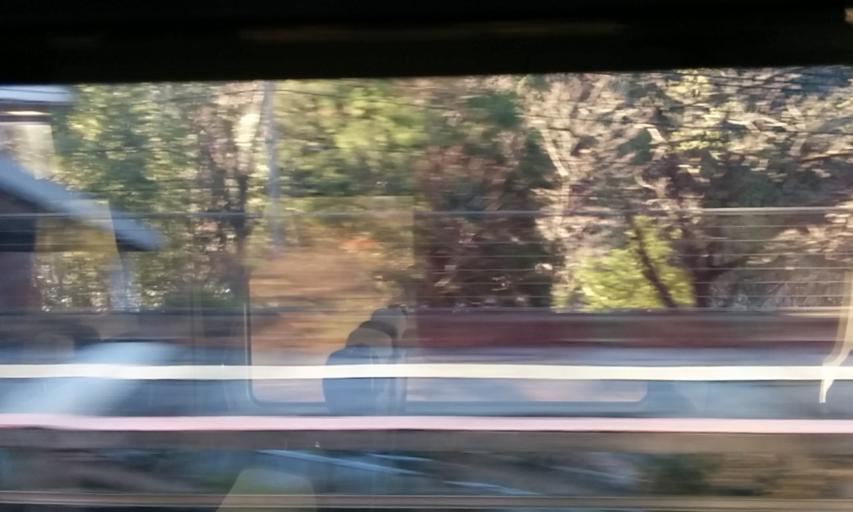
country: JP
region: Gifu
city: Nakatsugawa
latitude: 35.6453
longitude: 137.6176
